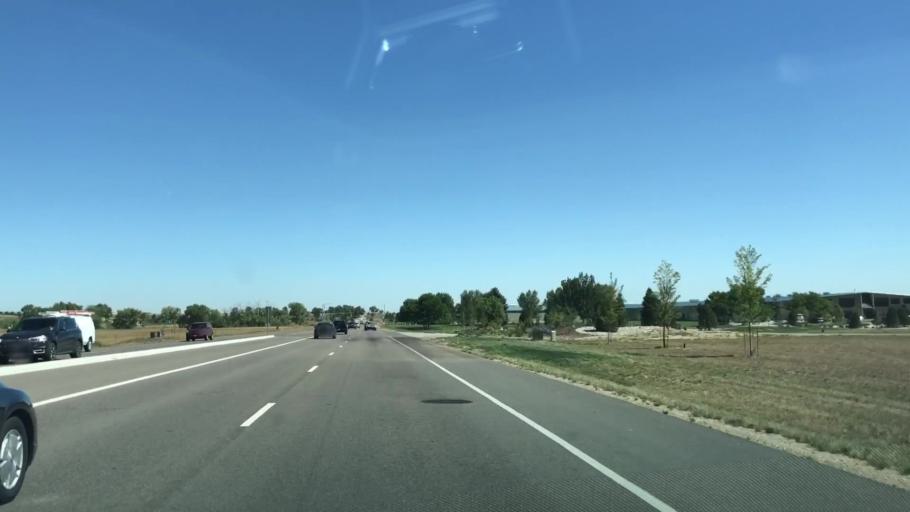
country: US
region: Colorado
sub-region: Weld County
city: Windsor
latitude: 40.5228
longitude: -104.9692
